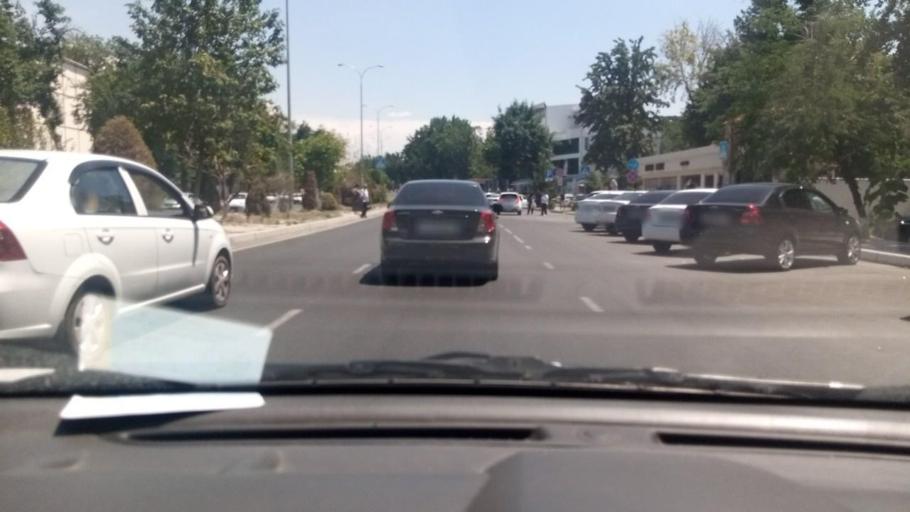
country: UZ
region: Toshkent Shahri
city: Tashkent
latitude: 41.2895
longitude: 69.2013
